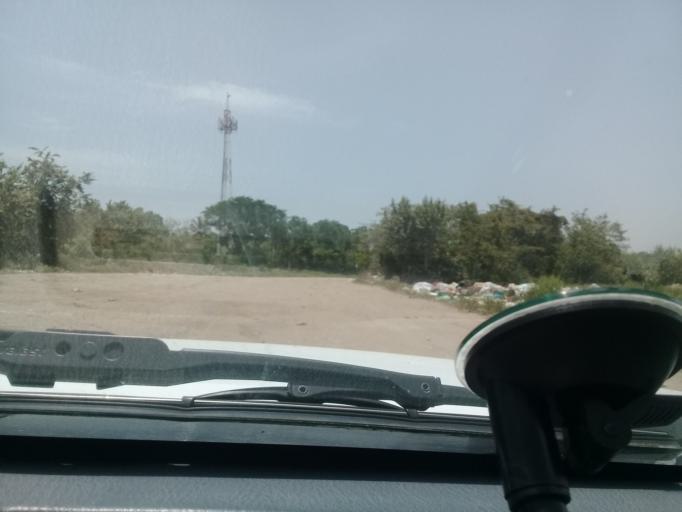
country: MX
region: Veracruz
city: Anahuac
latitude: 22.2229
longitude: -97.8241
